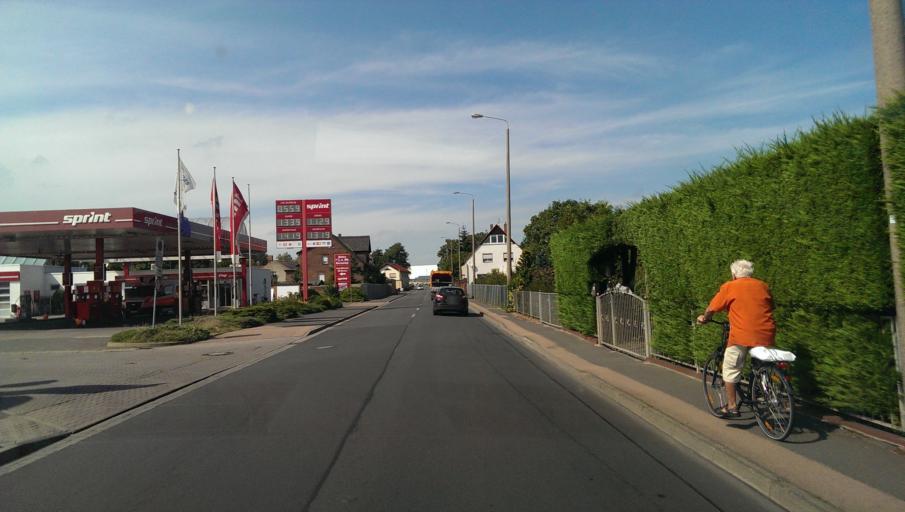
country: DE
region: Saxony-Anhalt
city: Wittenburg
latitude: 51.8737
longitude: 12.6341
